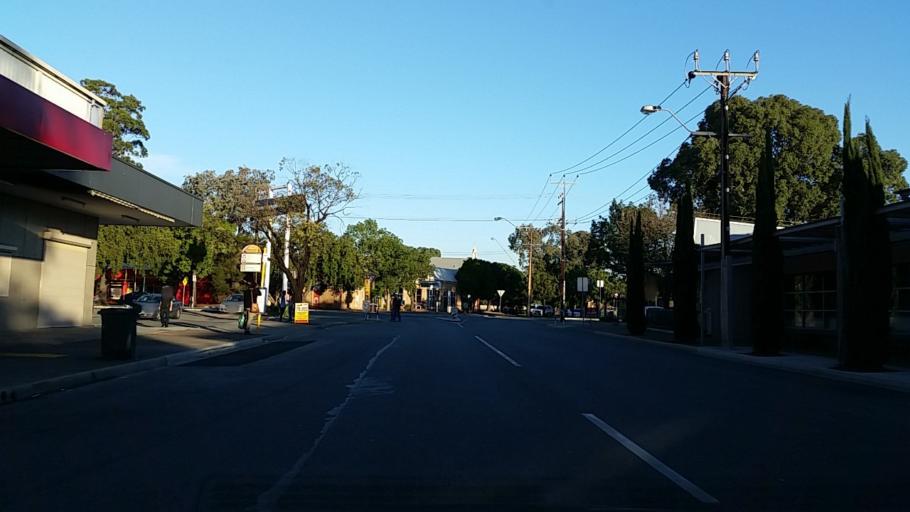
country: AU
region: South Australia
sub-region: Salisbury
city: Salisbury
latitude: -34.7627
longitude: 138.6455
